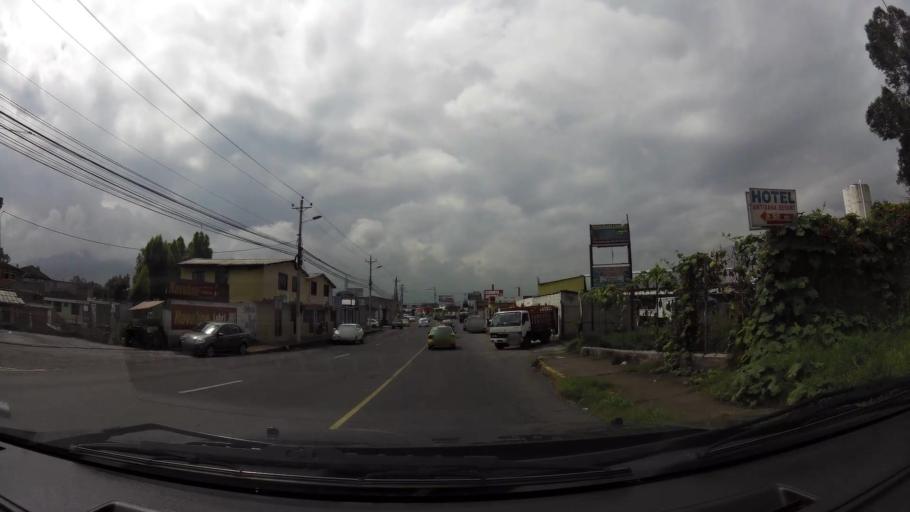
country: EC
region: Pichincha
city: Sangolqui
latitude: -0.3059
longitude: -78.4720
